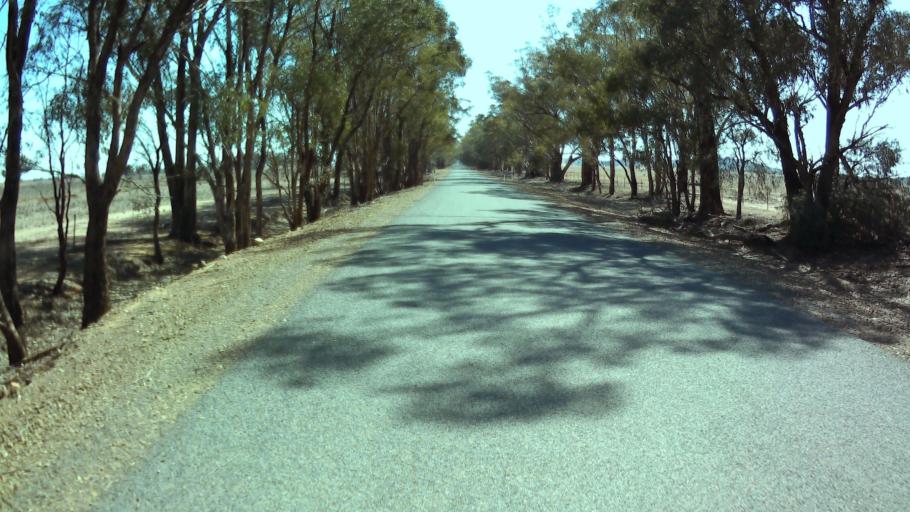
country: AU
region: New South Wales
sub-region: Weddin
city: Grenfell
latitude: -33.7277
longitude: 147.8916
